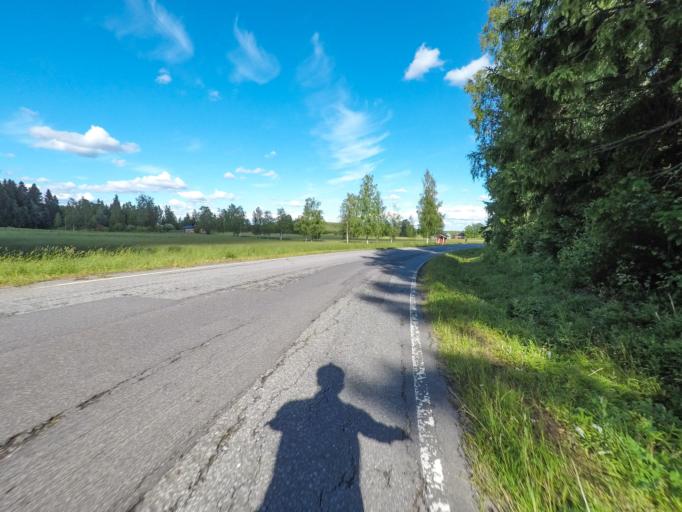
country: FI
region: South Karelia
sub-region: Imatra
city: Imatra
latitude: 61.1413
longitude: 28.6383
